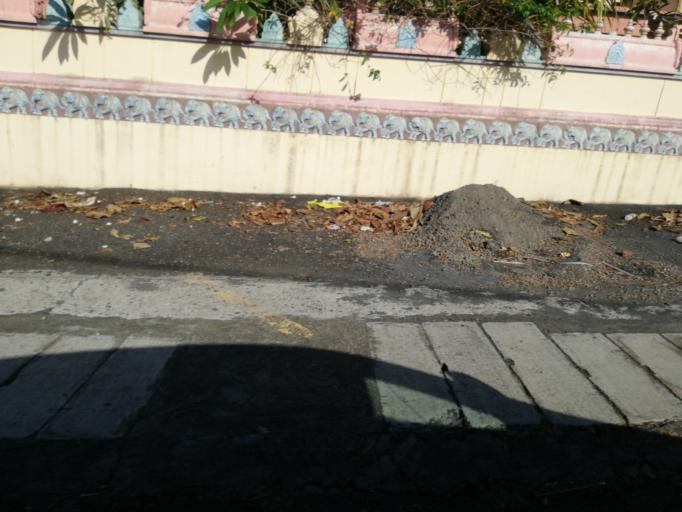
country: MU
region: Port Louis
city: Port Louis
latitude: -20.1615
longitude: 57.4887
